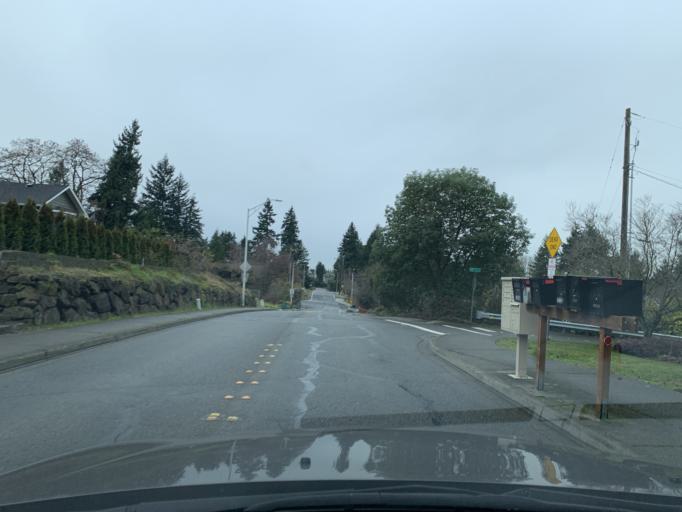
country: US
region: Washington
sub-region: King County
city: SeaTac
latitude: 47.4596
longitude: -122.2794
